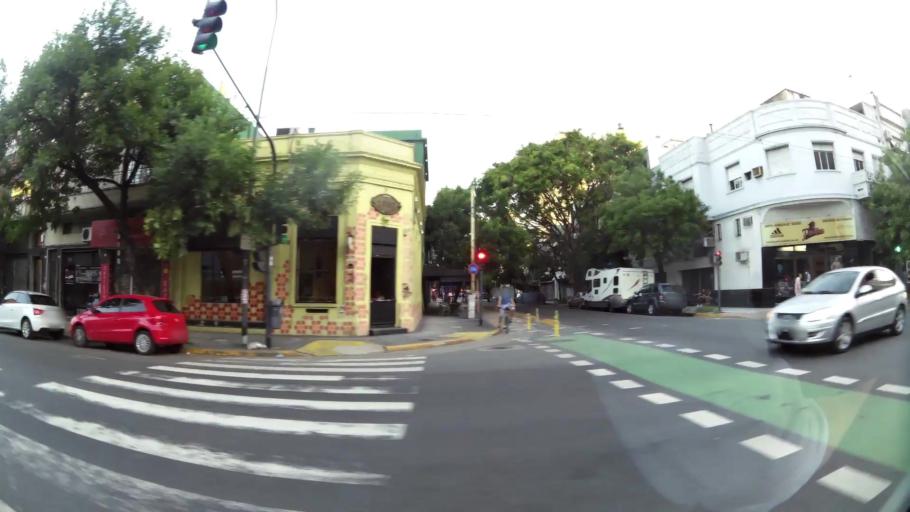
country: AR
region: Buenos Aires F.D.
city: Colegiales
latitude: -34.5971
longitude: -58.4345
